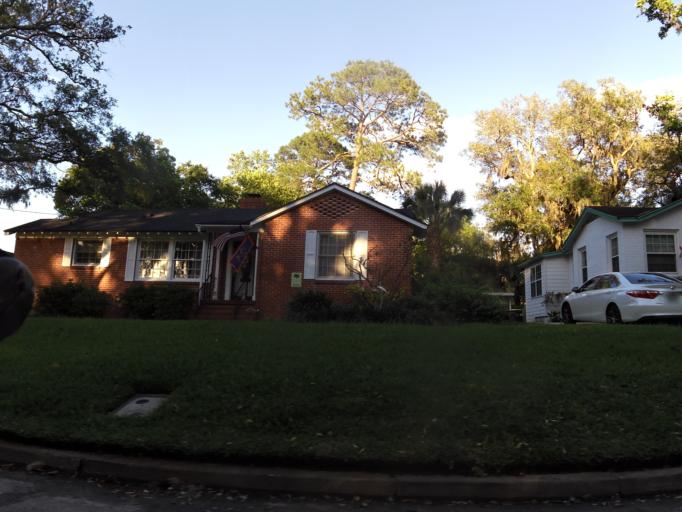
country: US
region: Florida
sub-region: Duval County
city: Jacksonville
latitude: 30.3093
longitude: -81.6377
